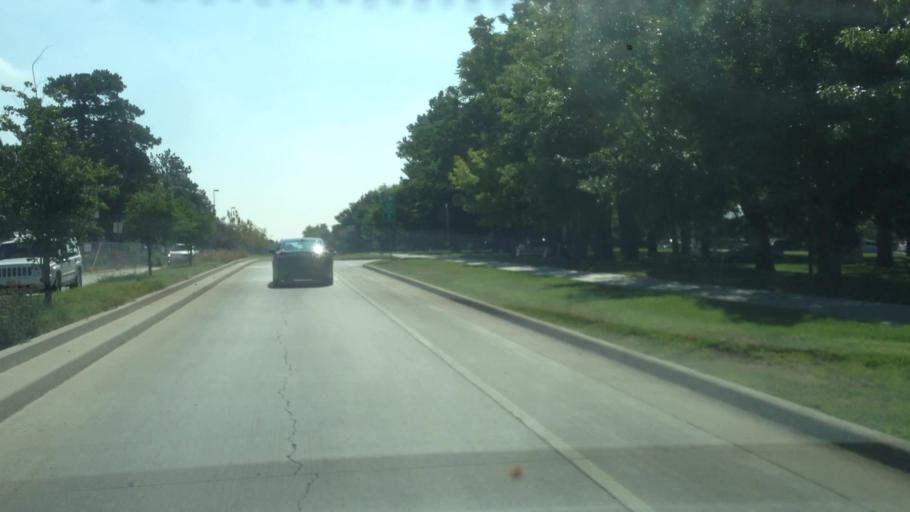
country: US
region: Colorado
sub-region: Denver County
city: Denver
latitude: 39.7512
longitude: -104.9480
